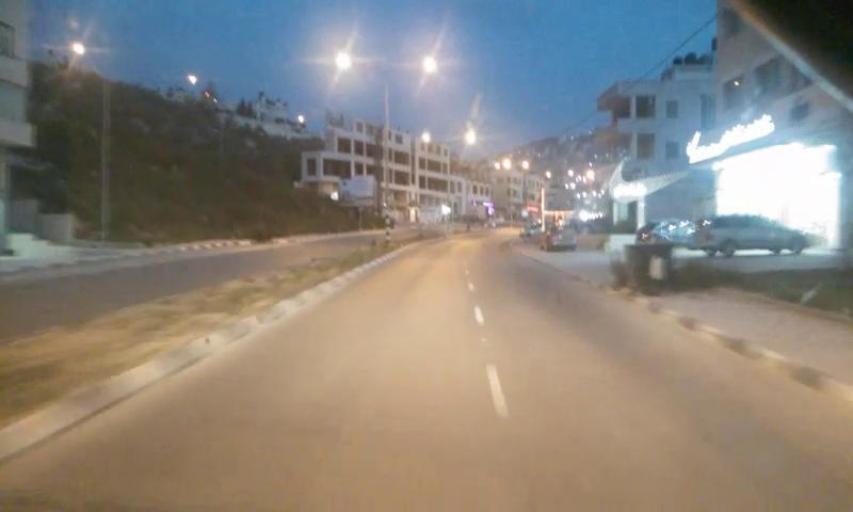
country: PS
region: West Bank
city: Zawata
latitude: 32.2379
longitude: 35.2328
